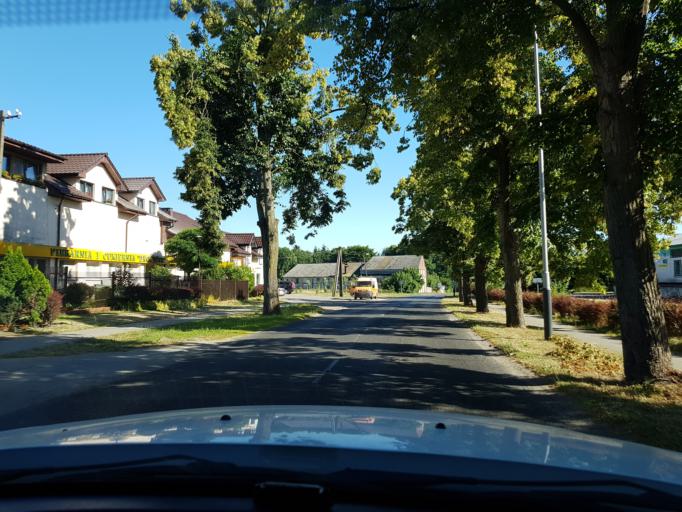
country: PL
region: West Pomeranian Voivodeship
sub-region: Powiat lobeski
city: Lobez
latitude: 53.6458
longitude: 15.6164
